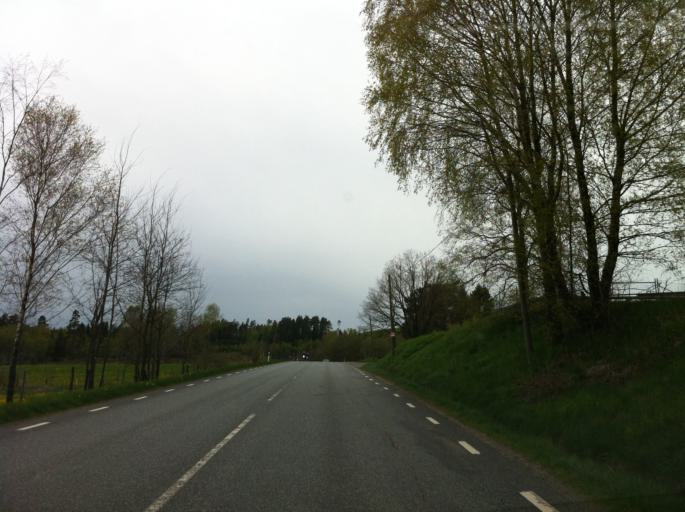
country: SE
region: Halland
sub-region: Falkenbergs Kommun
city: Falkenberg
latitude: 57.0621
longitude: 12.6398
